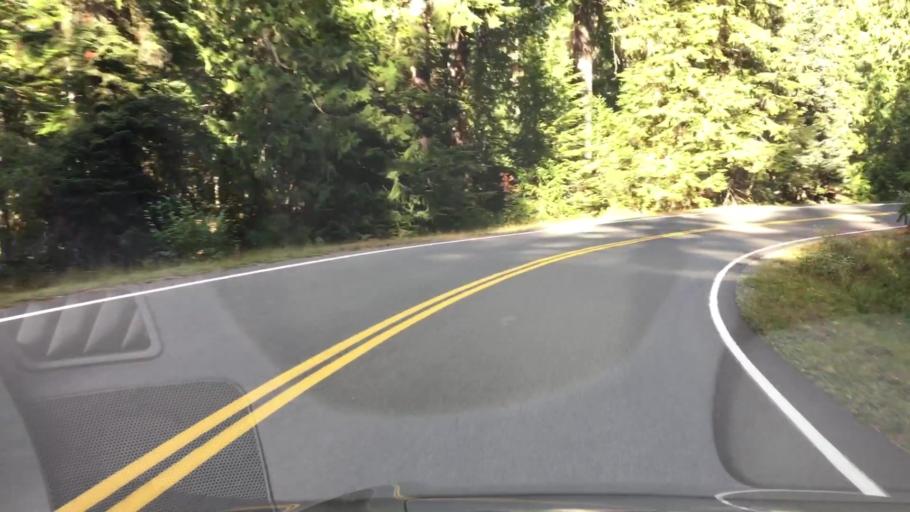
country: US
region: Washington
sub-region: Pierce County
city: Buckley
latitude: 46.7542
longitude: -121.5654
